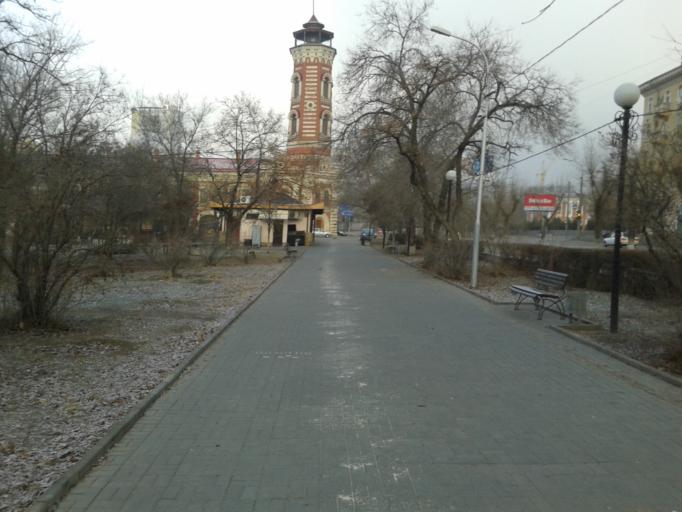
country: RU
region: Volgograd
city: Volgograd
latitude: 48.7091
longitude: 44.5117
